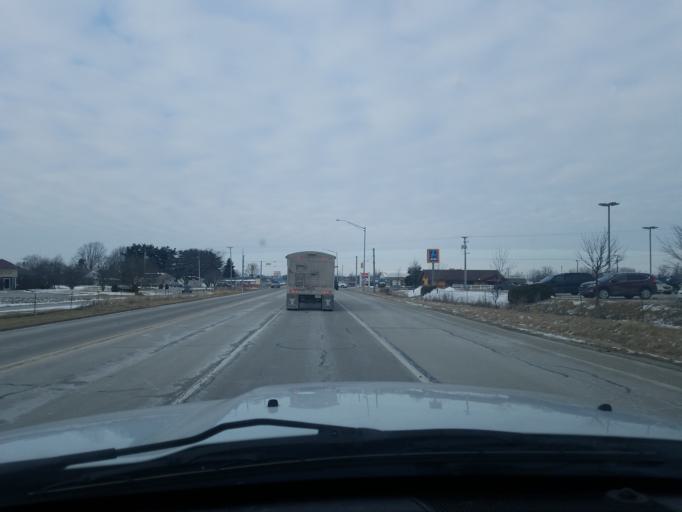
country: US
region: Indiana
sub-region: Randolph County
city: Winchester
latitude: 40.1647
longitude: -84.9670
